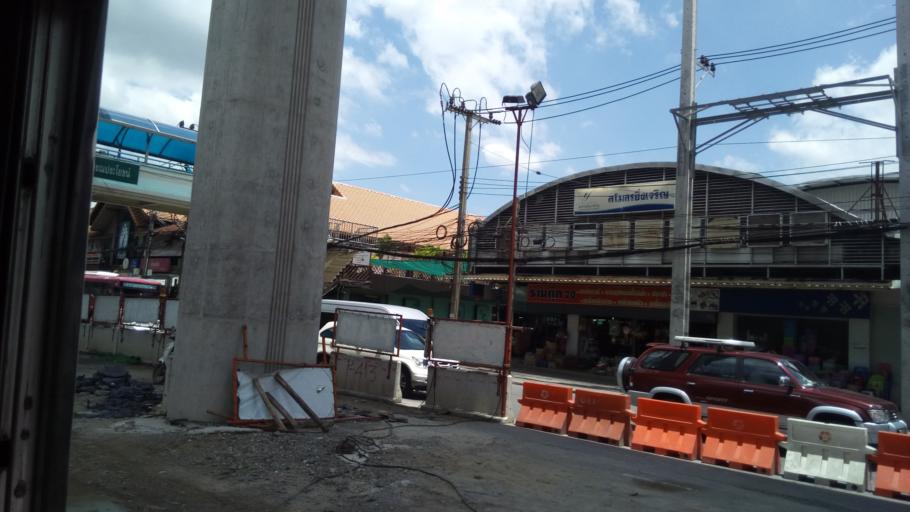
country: TH
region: Bangkok
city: Don Mueang
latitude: 13.8981
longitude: 100.6101
